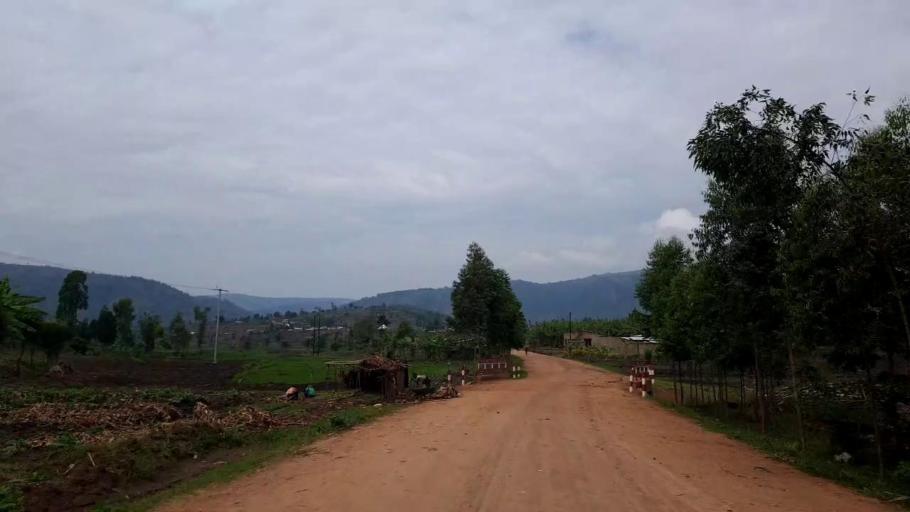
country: RW
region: Northern Province
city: Byumba
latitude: -1.4984
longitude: 30.2208
